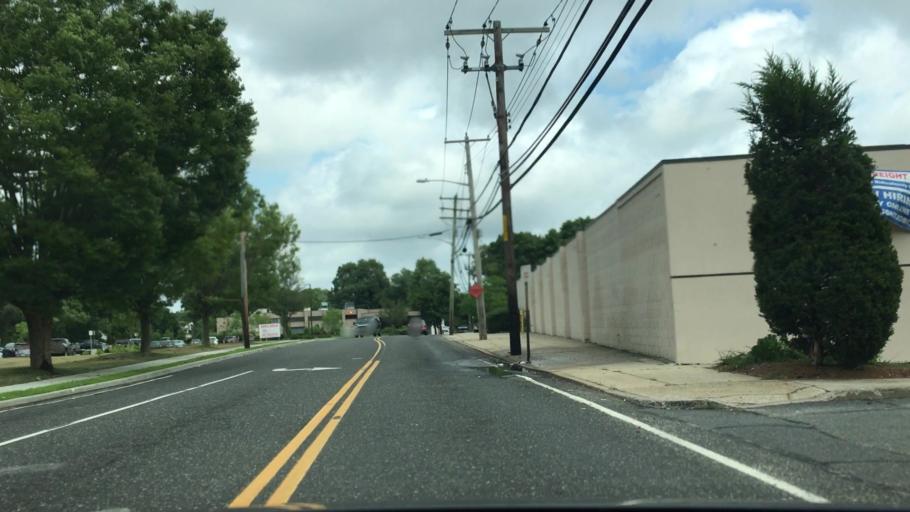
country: US
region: New York
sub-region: Suffolk County
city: West Hills
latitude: 40.8289
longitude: -73.4211
